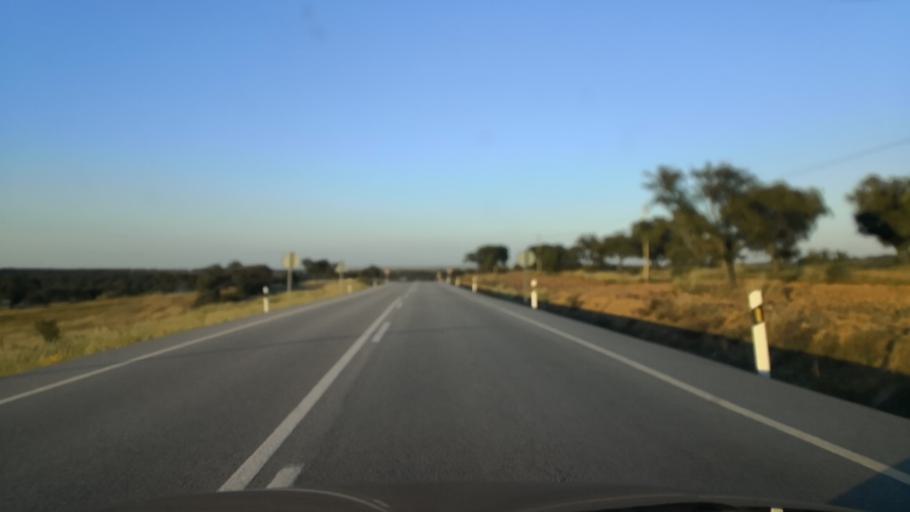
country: ES
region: Extremadura
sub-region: Provincia de Caceres
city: Salorino
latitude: 39.5110
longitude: -7.0943
